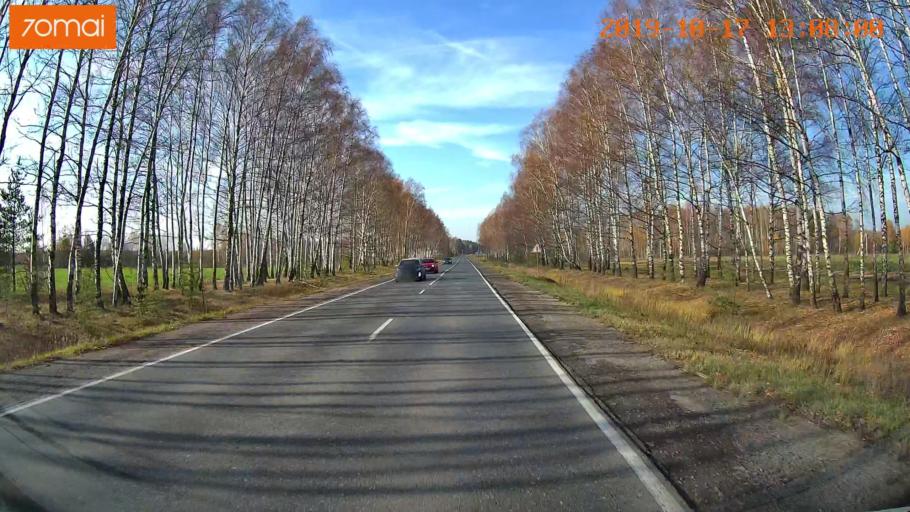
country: RU
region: Rjazan
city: Syntul
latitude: 54.9860
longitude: 41.2776
